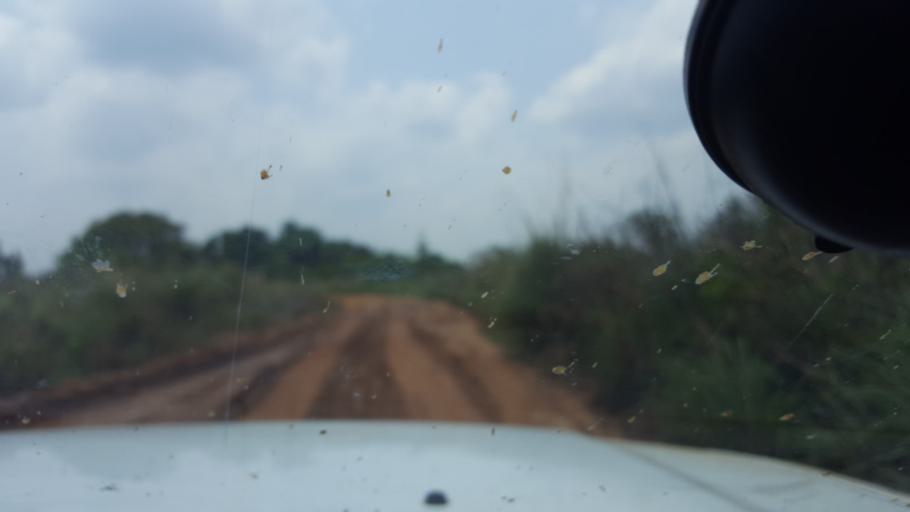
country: CD
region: Bandundu
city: Mushie
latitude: -3.7508
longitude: 16.6467
